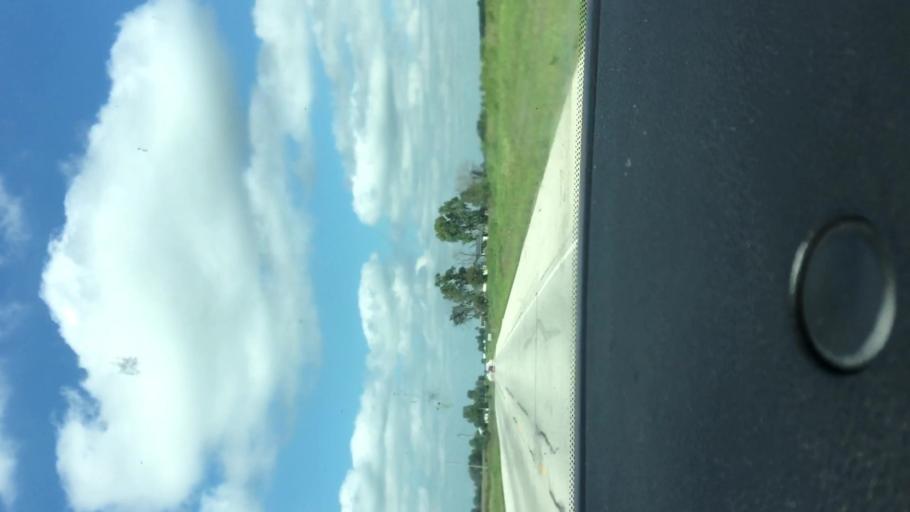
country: US
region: Indiana
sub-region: Jay County
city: Portland
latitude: 40.3541
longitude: -84.9775
